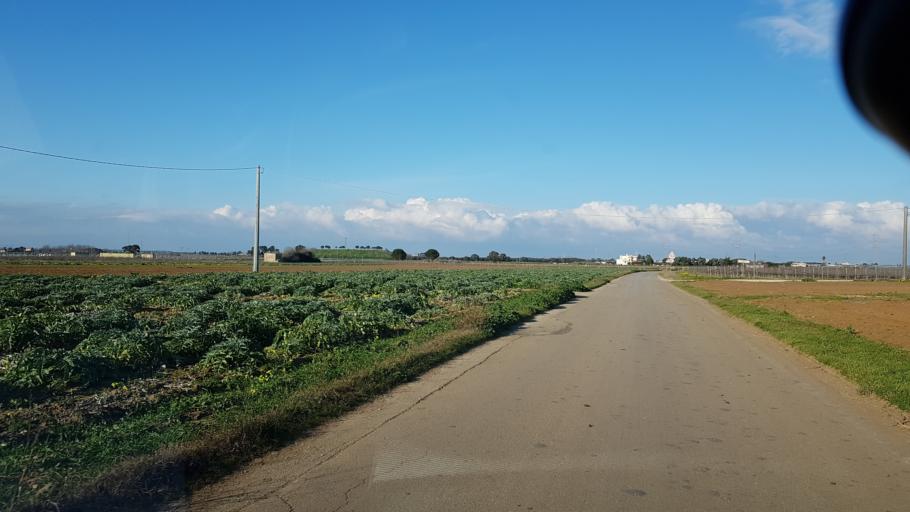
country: IT
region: Apulia
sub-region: Provincia di Brindisi
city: Tuturano
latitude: 40.5732
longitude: 17.8997
